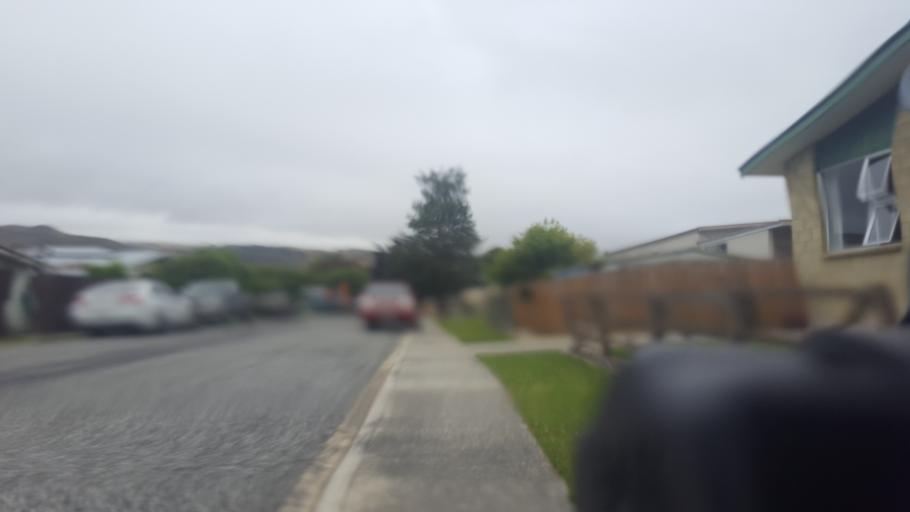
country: NZ
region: Otago
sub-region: Queenstown-Lakes District
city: Kingston
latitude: -45.5352
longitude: 169.3059
